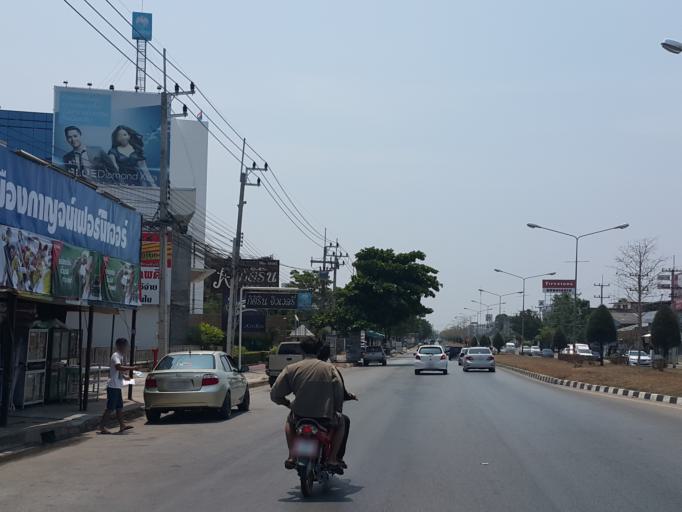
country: TH
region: Kanchanaburi
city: Kanchanaburi
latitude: 14.0456
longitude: 99.5104
